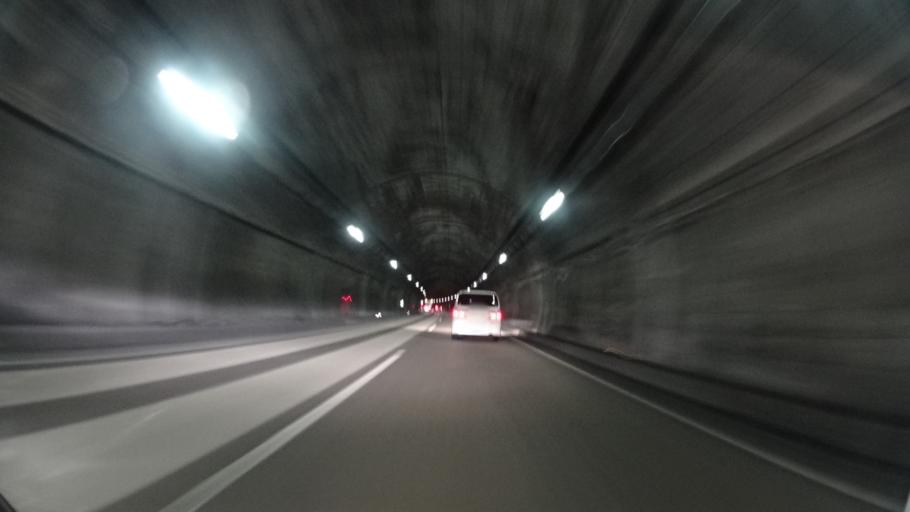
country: JP
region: Hyogo
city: Himeji
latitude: 34.8552
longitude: 134.7288
